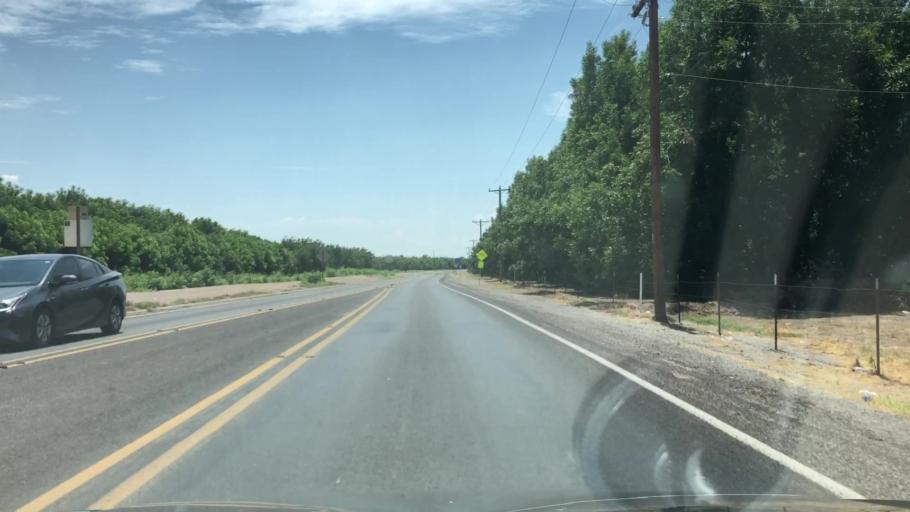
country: US
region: New Mexico
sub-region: Dona Ana County
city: La Union
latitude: 31.9957
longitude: -106.6543
